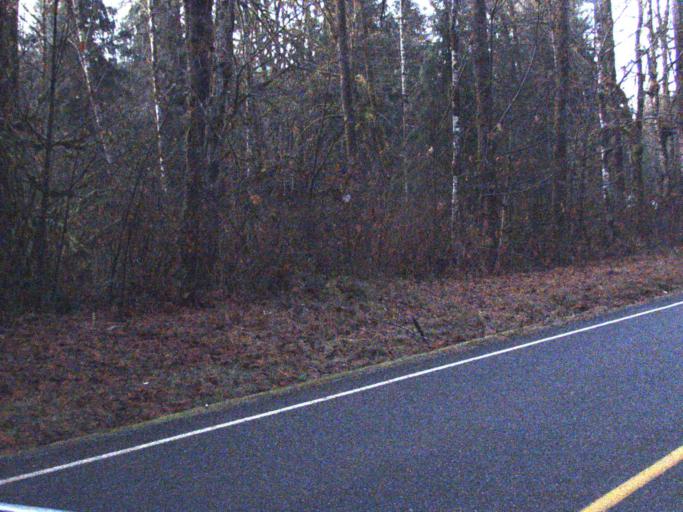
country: US
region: Washington
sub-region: Snohomish County
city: Darrington
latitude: 48.4269
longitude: -121.5654
